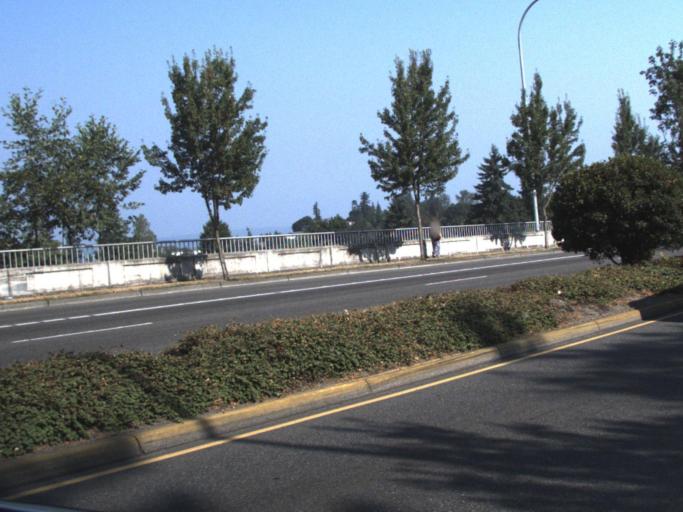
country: US
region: Washington
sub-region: King County
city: Federal Way
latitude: 47.3501
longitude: -122.3123
